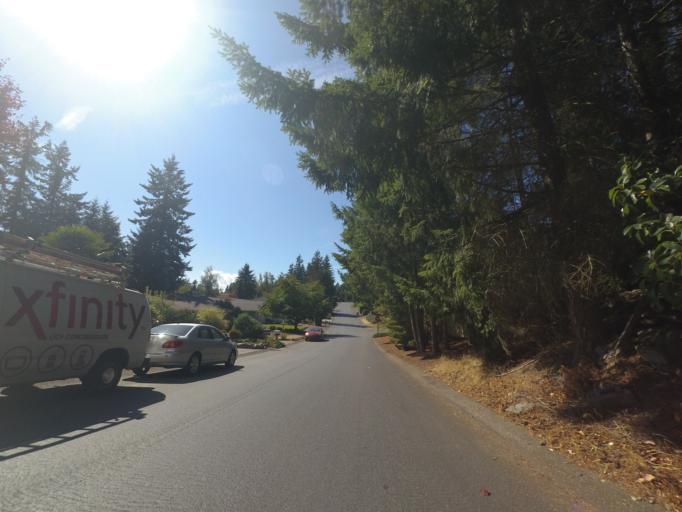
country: US
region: Washington
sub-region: Pierce County
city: Fircrest
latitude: 47.2105
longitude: -122.5169
